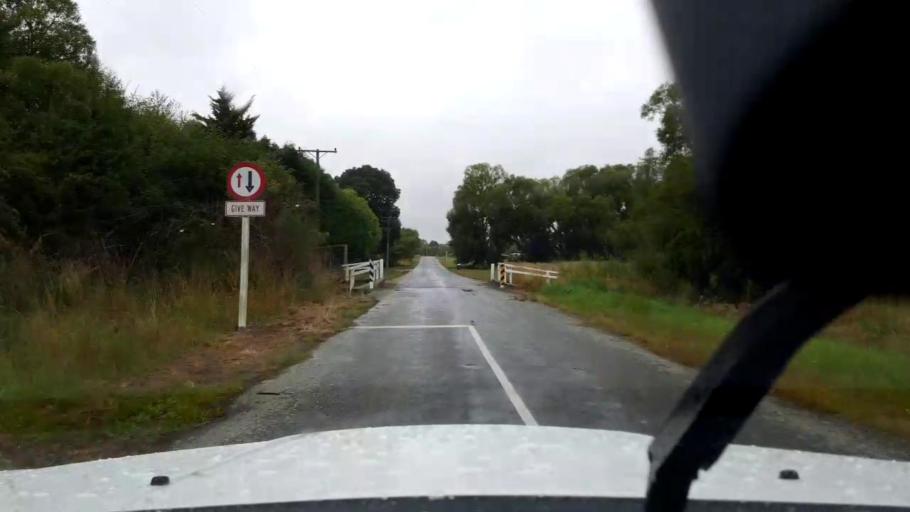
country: NZ
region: Canterbury
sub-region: Timaru District
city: Pleasant Point
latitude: -44.2522
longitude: 171.2556
